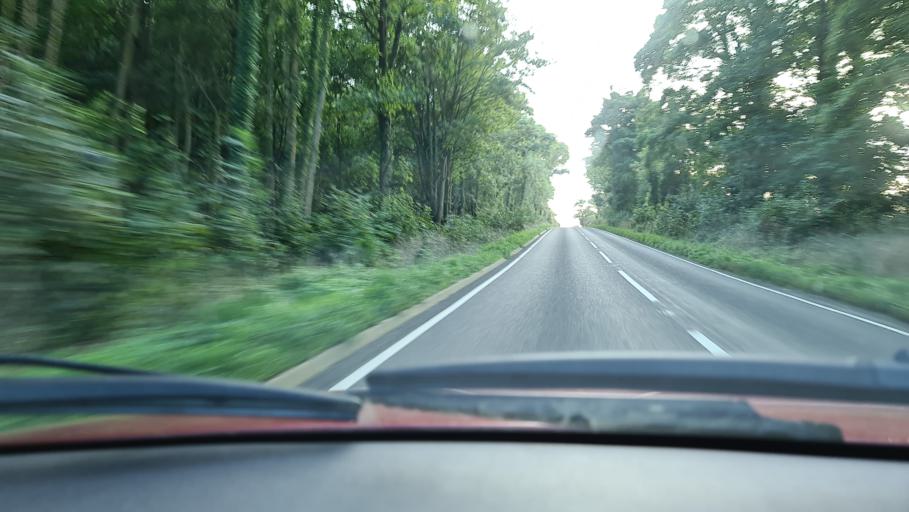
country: GB
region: England
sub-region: Oxfordshire
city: Somerton
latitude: 51.8918
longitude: -1.2428
